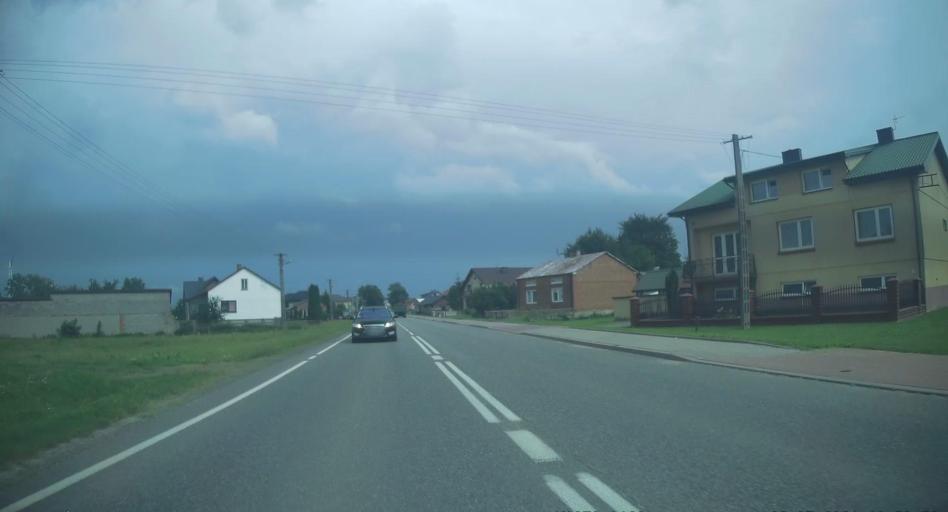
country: PL
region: Lodz Voivodeship
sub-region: Powiat skierniewicki
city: Gluchow
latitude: 51.7726
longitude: 20.1394
